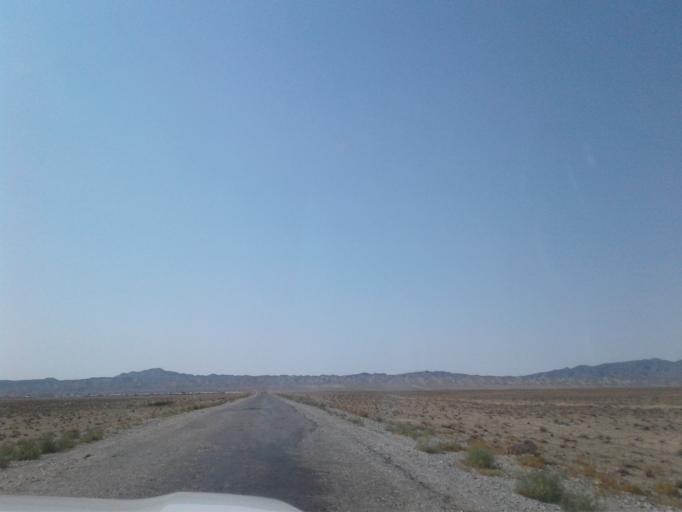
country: TM
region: Balkan
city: Gazanjyk
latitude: 39.1765
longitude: 55.3059
